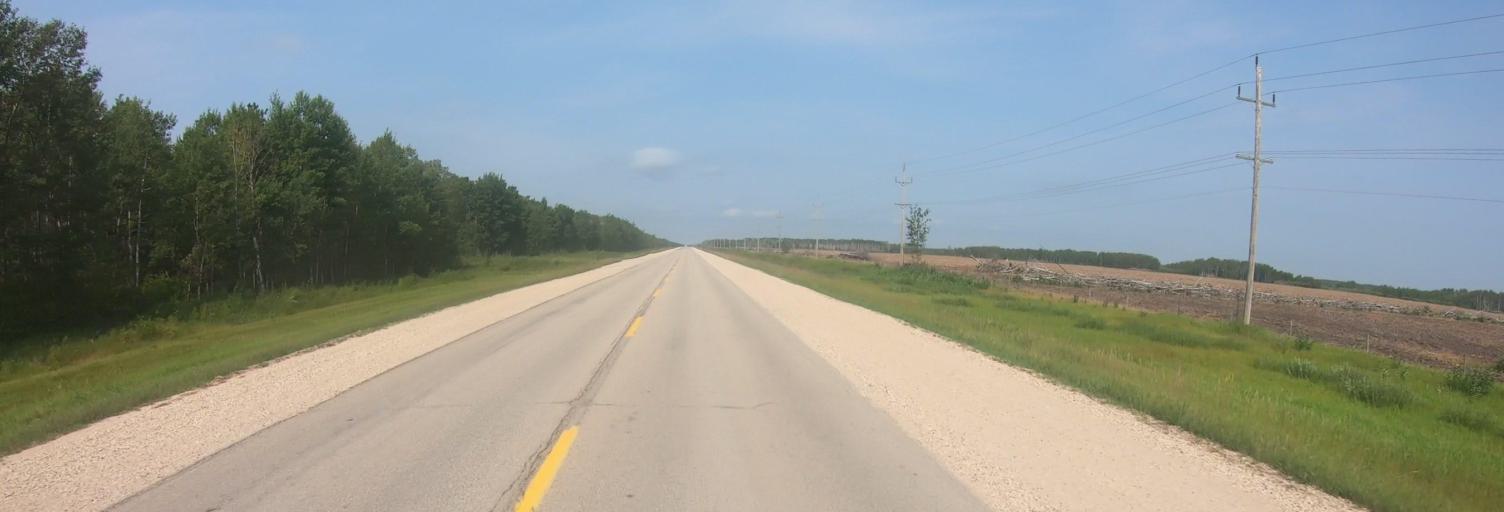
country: CA
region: Manitoba
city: Steinbach
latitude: 49.3300
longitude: -96.6075
